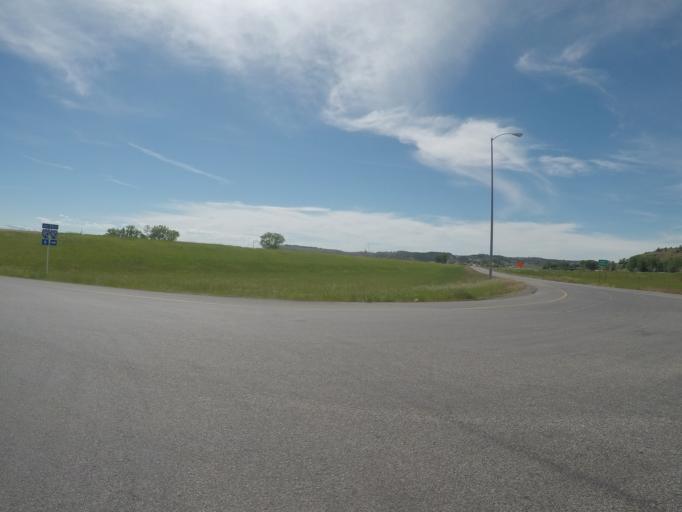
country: US
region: Montana
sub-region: Stillwater County
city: Columbus
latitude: 45.6478
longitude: -109.2473
